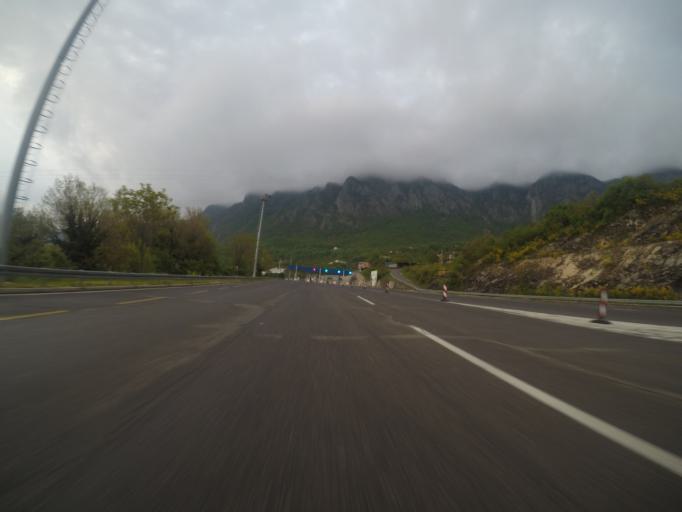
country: ME
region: Bar
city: Sutomore
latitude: 42.2019
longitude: 19.0512
